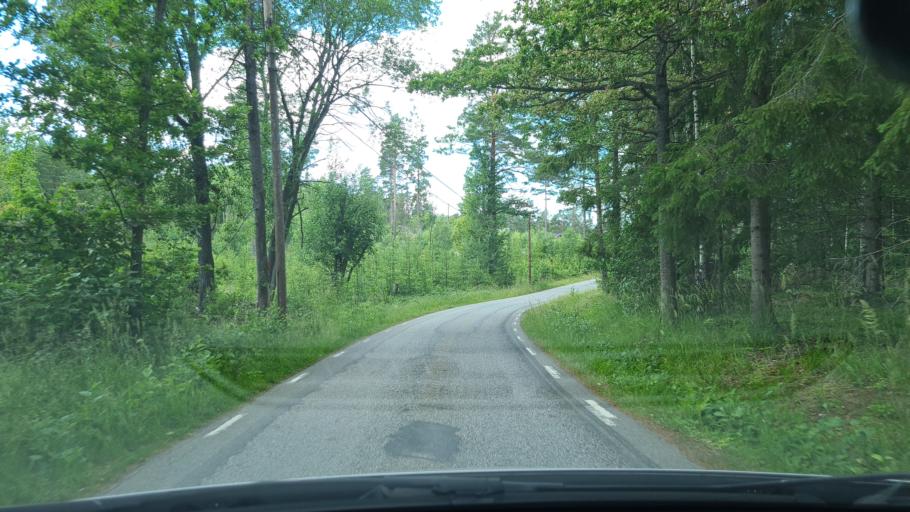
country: SE
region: Stockholm
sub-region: Vaxholms Kommun
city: Vaxholm
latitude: 59.4180
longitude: 18.4331
